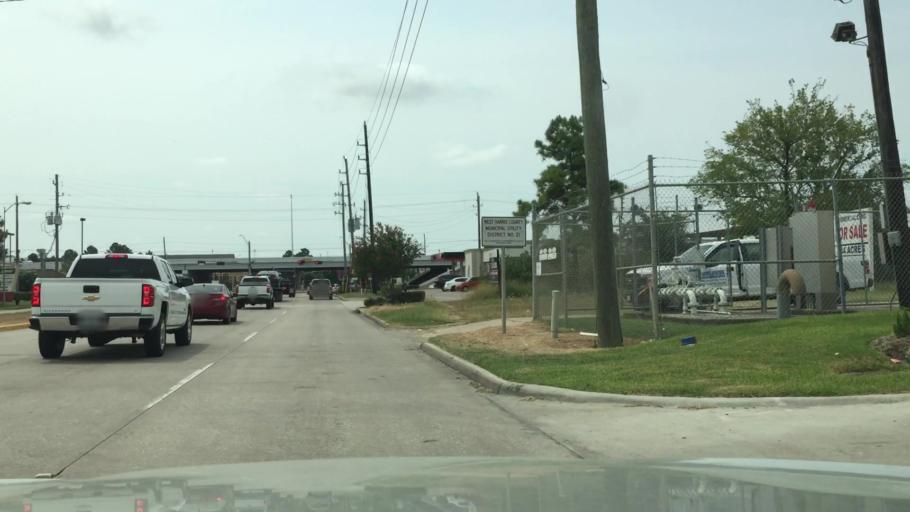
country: US
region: Texas
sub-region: Harris County
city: Jersey Village
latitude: 29.9316
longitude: -95.5453
